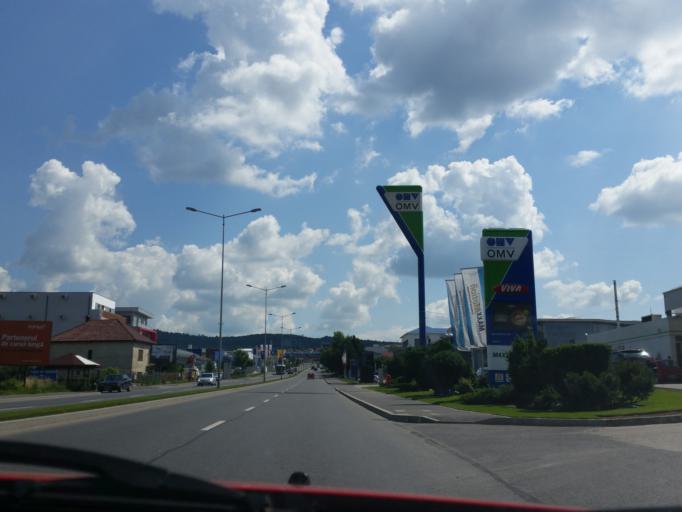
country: RO
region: Cluj
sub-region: Municipiul Cluj-Napoca
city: Cluj-Napoca
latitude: 46.7448
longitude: 23.5923
